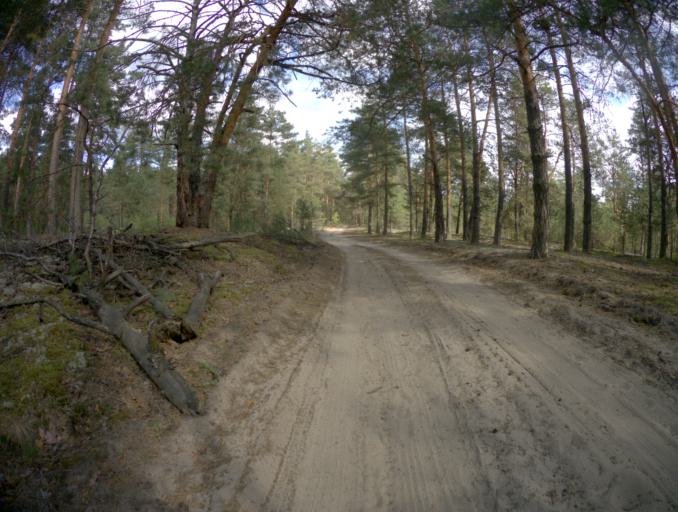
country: RU
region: Vladimir
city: Petushki
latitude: 55.8617
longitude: 39.3694
